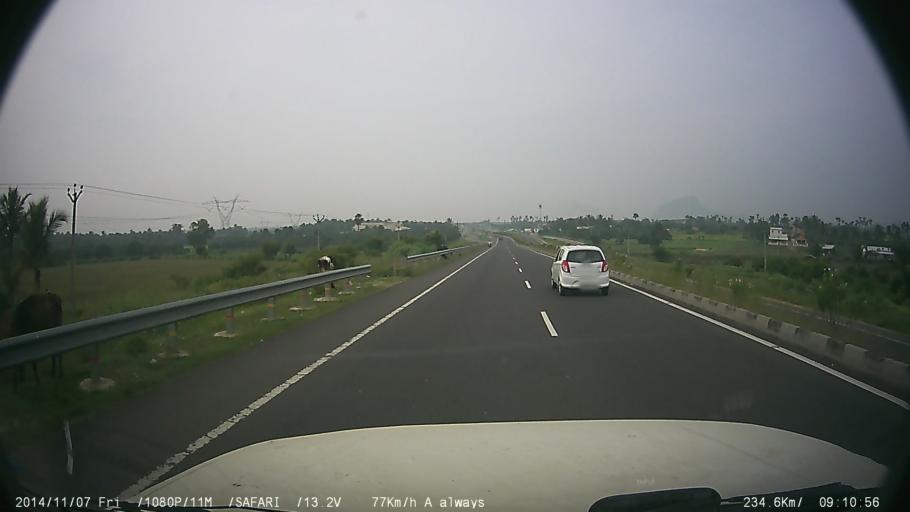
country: IN
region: Tamil Nadu
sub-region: Salem
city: Konganapuram
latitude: 11.5043
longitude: 77.9137
